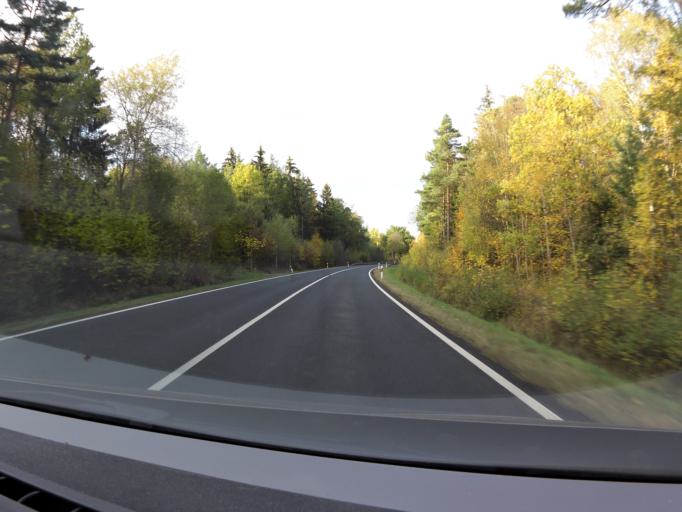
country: DE
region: Thuringia
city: Luisenthal
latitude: 50.7941
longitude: 10.7503
